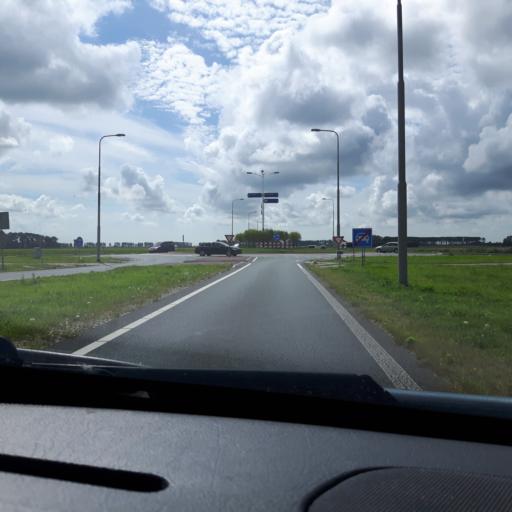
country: NL
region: Zeeland
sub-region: Gemeente Noord-Beveland
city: Kamperland
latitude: 51.5769
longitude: 3.7586
